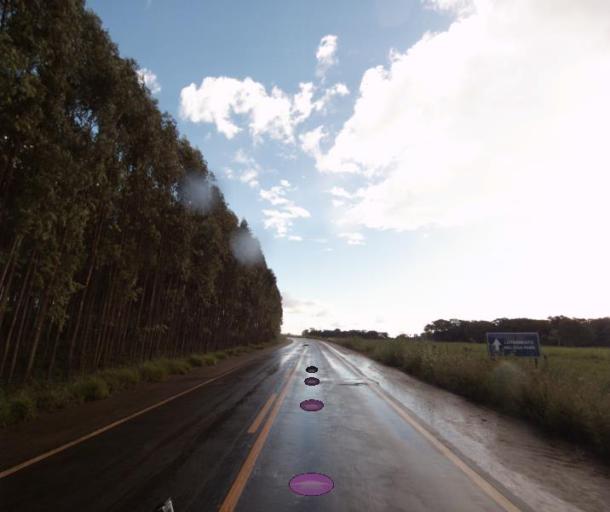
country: BR
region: Goias
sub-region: Itaberai
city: Itaberai
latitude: -16.0128
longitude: -49.7676
